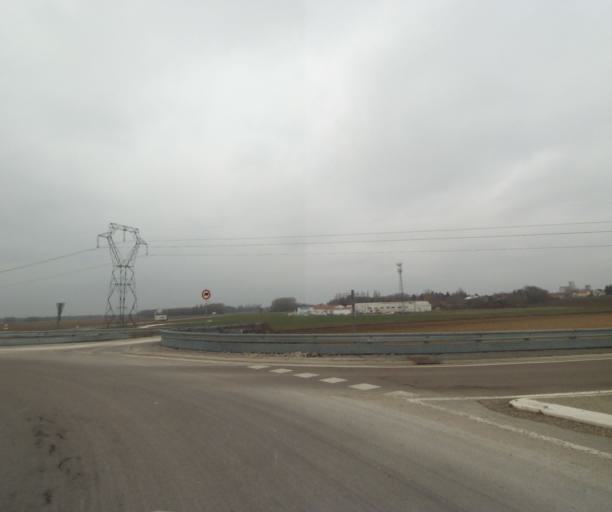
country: FR
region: Champagne-Ardenne
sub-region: Departement de la Marne
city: Pargny-sur-Saulx
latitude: 48.6846
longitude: 4.7409
